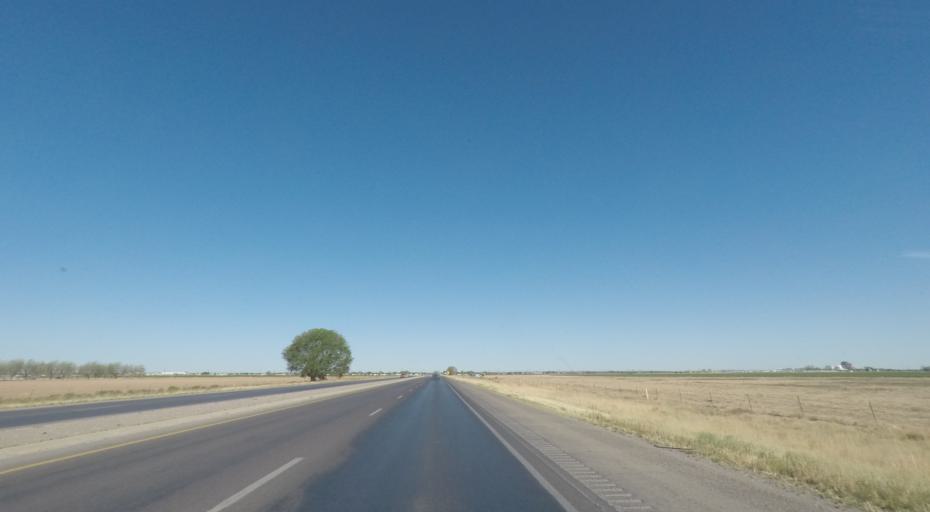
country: US
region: New Mexico
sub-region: Chaves County
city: Roswell
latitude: 33.3082
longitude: -104.4733
